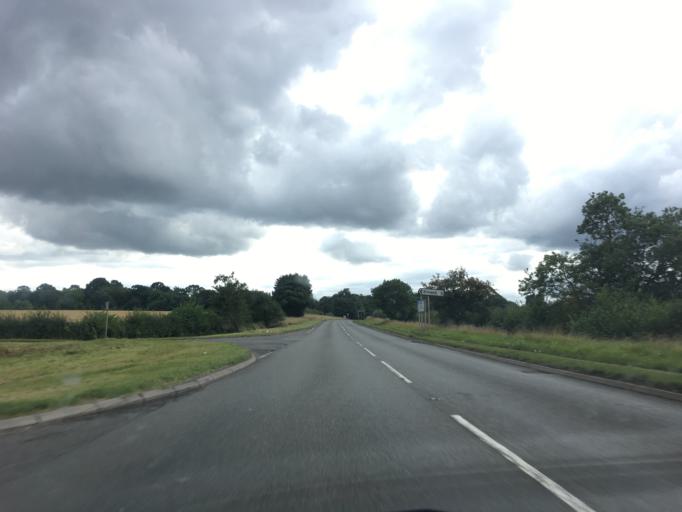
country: GB
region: England
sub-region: Leicestershire
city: Lutterworth
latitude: 52.4401
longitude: -1.1999
